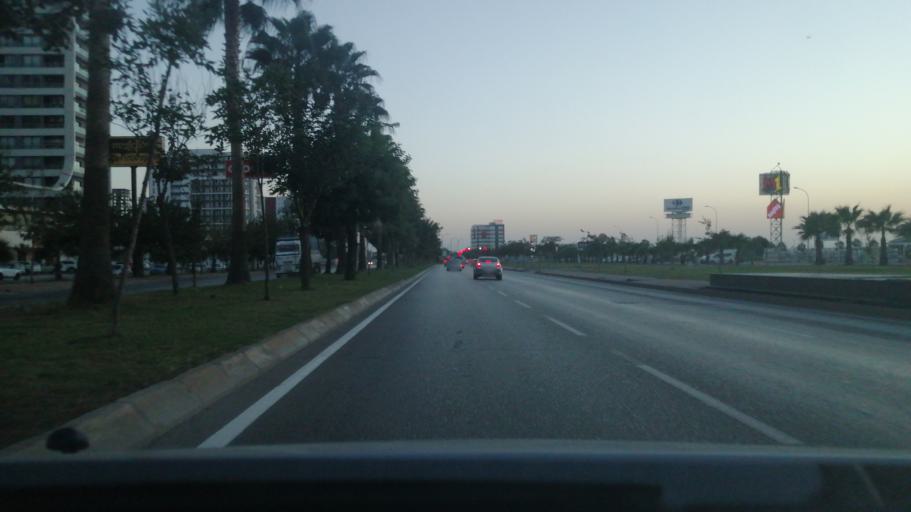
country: TR
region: Adana
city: Seyhan
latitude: 37.0187
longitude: 35.2520
